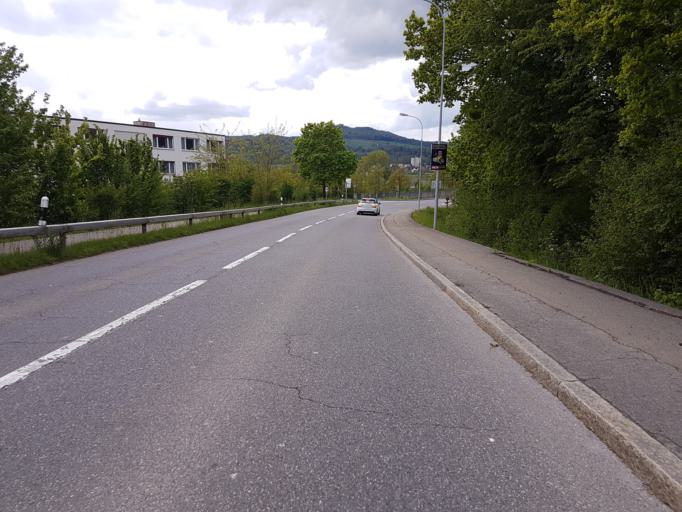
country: CH
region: Aargau
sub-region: Bezirk Brugg
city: Schinznach Bad
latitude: 47.4452
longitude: 8.1665
